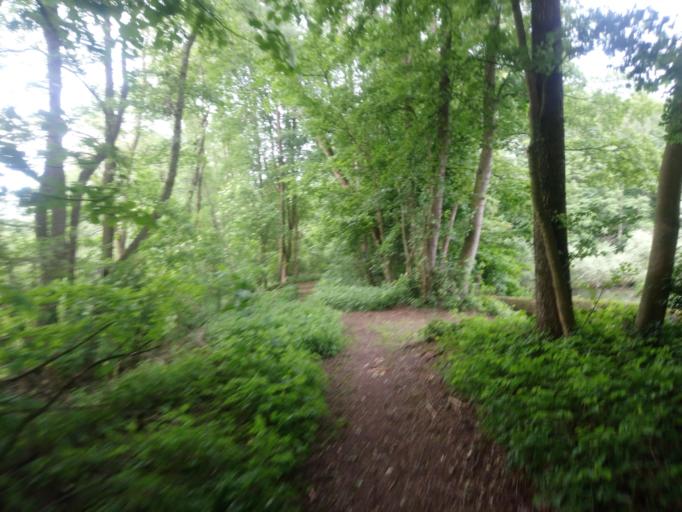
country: DE
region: North Rhine-Westphalia
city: Bad Lippspringe
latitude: 51.7807
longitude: 8.7858
